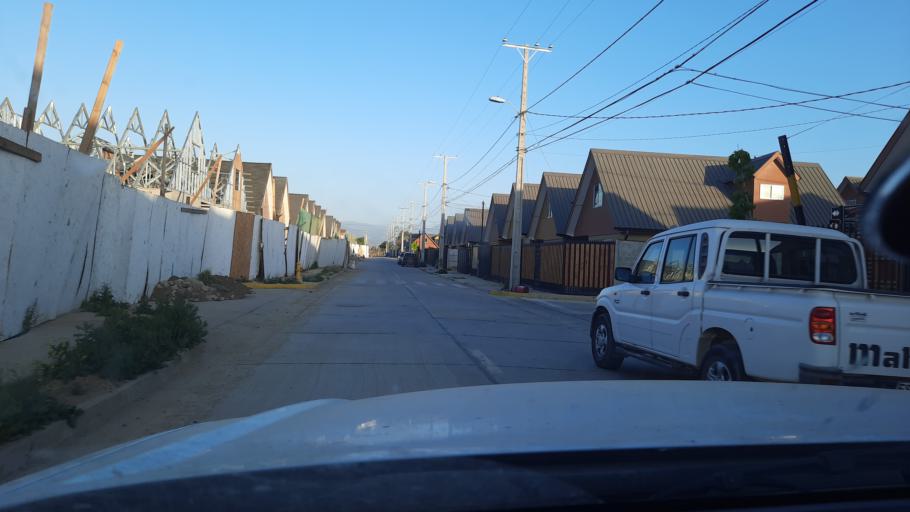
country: CL
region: Valparaiso
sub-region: Provincia de Marga Marga
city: Limache
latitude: -32.9953
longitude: -71.2783
